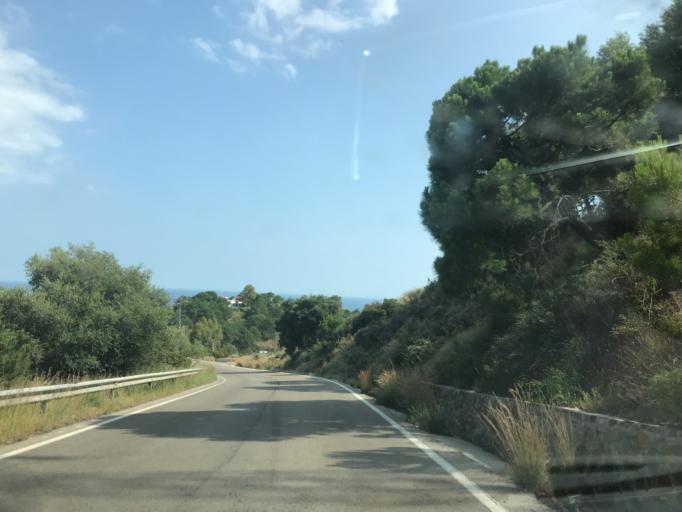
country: ES
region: Andalusia
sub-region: Provincia de Malaga
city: Estepona
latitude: 36.4476
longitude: -5.1537
